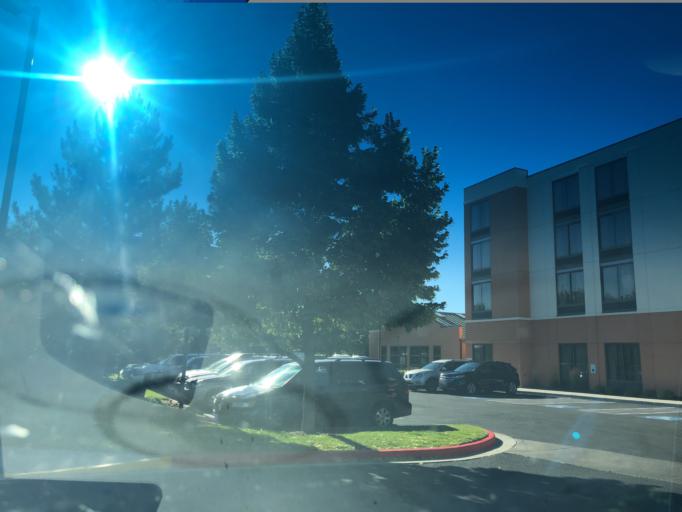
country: US
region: Idaho
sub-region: Ada County
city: Garden City
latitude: 43.6130
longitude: -116.2856
